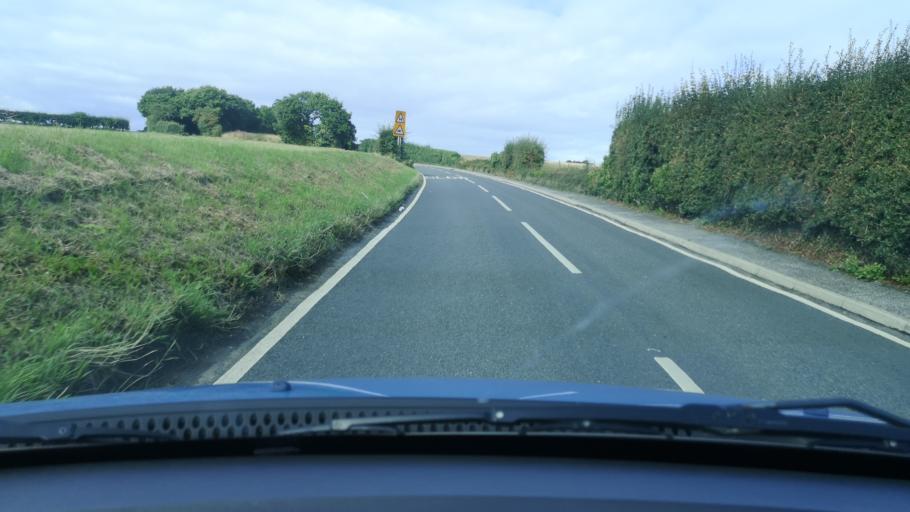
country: GB
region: England
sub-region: City and Borough of Wakefield
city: Horbury
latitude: 53.6440
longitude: -1.5544
